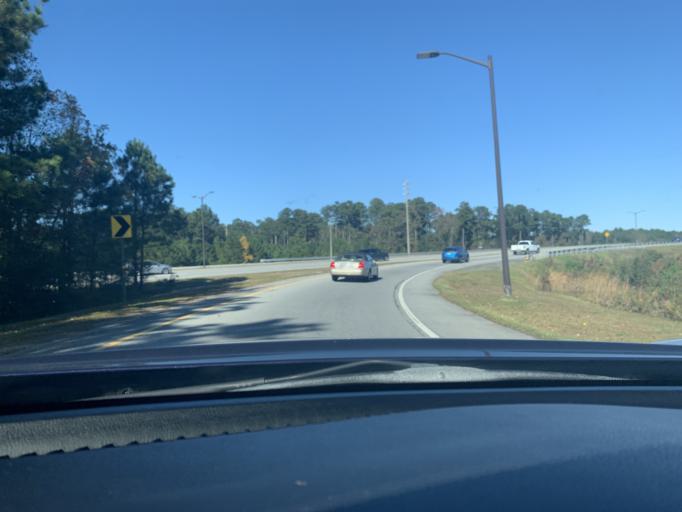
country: US
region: Georgia
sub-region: Chatham County
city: Pooler
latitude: 32.1190
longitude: -81.2683
